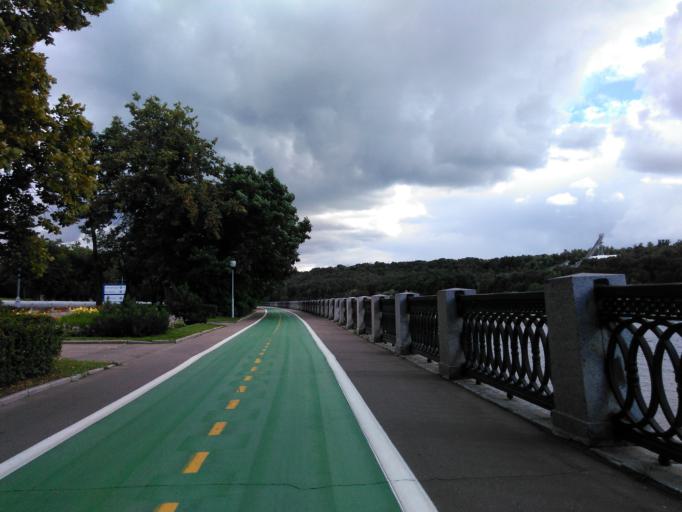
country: RU
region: Moscow
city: Luzhniki
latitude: 55.7167
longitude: 37.5445
